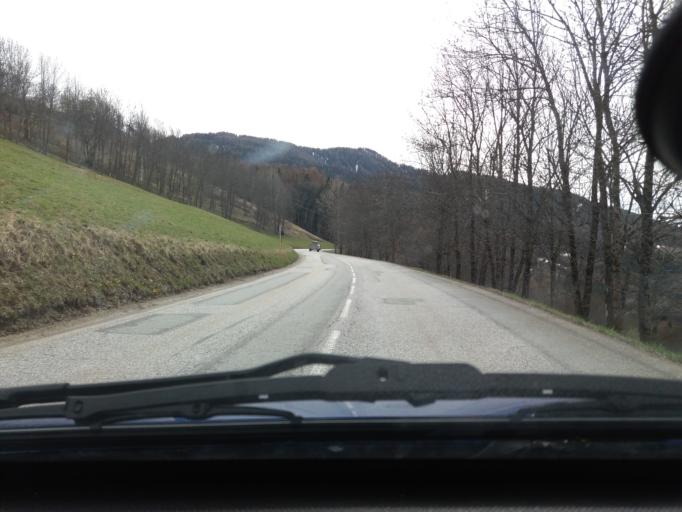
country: FR
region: Rhone-Alpes
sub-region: Departement de la Savoie
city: Macot-la-Plagne
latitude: 45.5427
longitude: 6.6708
